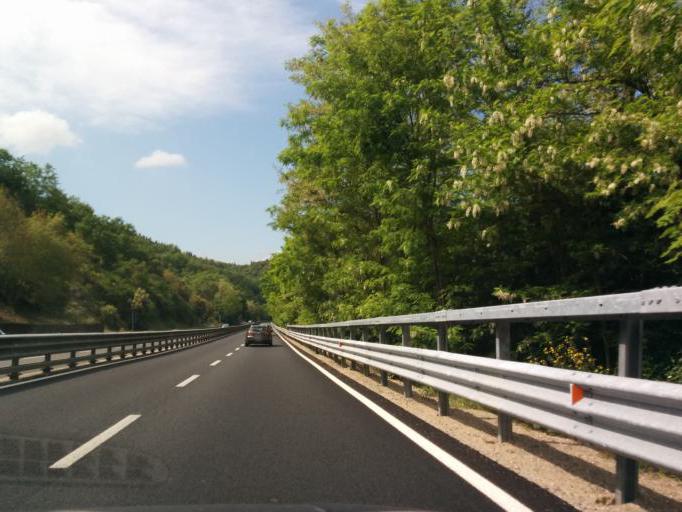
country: IT
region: Tuscany
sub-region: Province of Florence
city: Barberino Val d'Elsa
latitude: 43.5053
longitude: 11.1889
